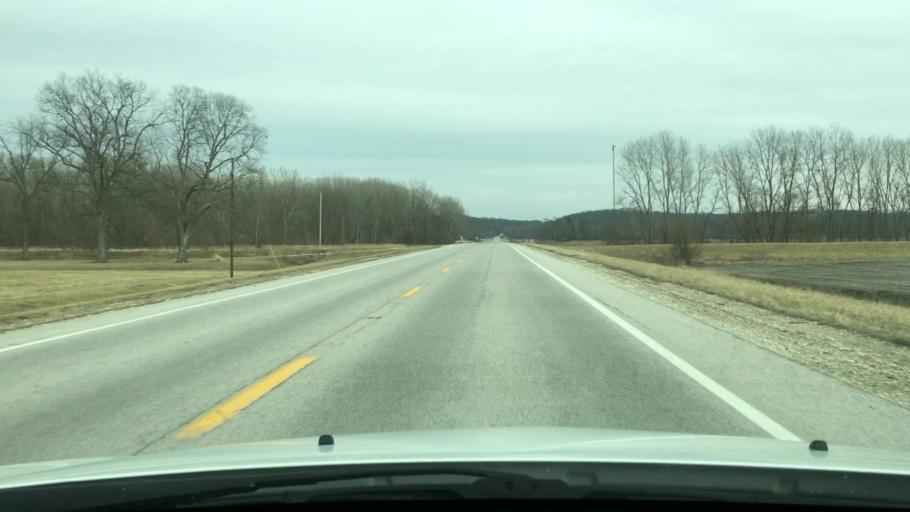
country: US
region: Missouri
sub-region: Pike County
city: Louisiana
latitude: 39.5022
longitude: -90.9911
